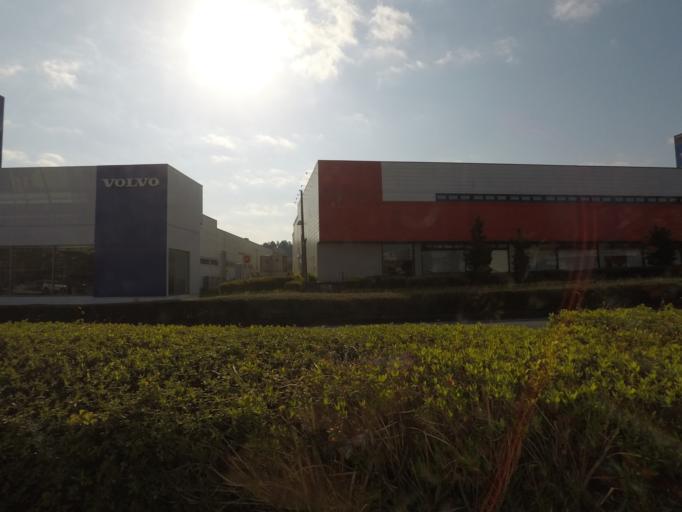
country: JP
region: Chiba
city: Narita
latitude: 35.7724
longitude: 140.3147
